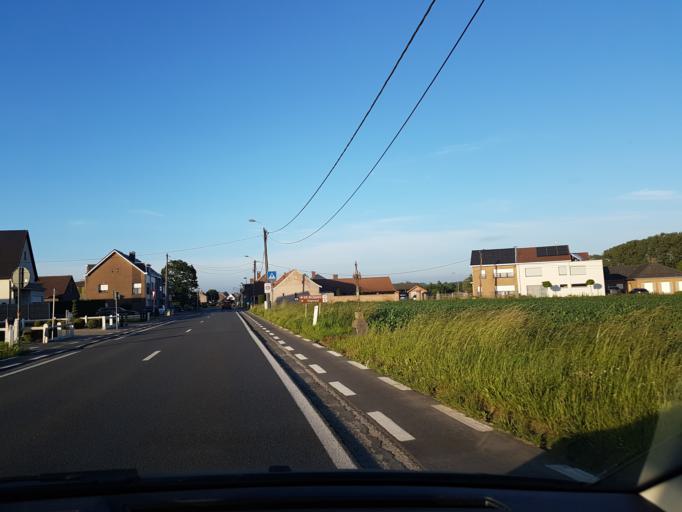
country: BE
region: Flanders
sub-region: Provincie Vlaams-Brabant
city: Opwijk
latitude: 50.9598
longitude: 4.1999
